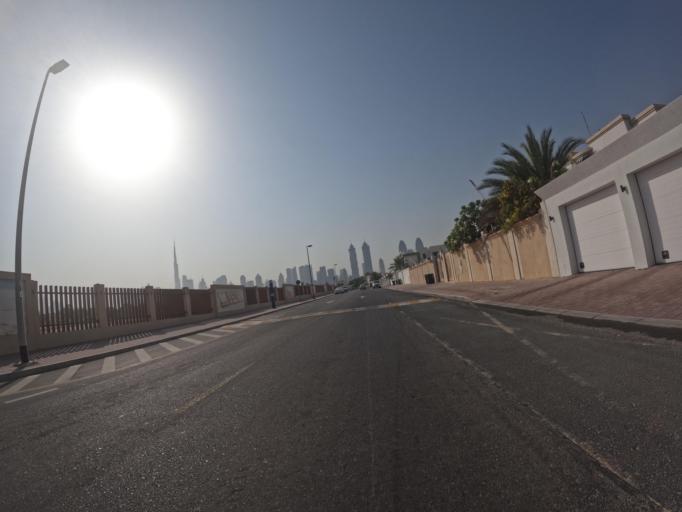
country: AE
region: Dubai
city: Dubai
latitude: 25.1956
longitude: 55.2405
